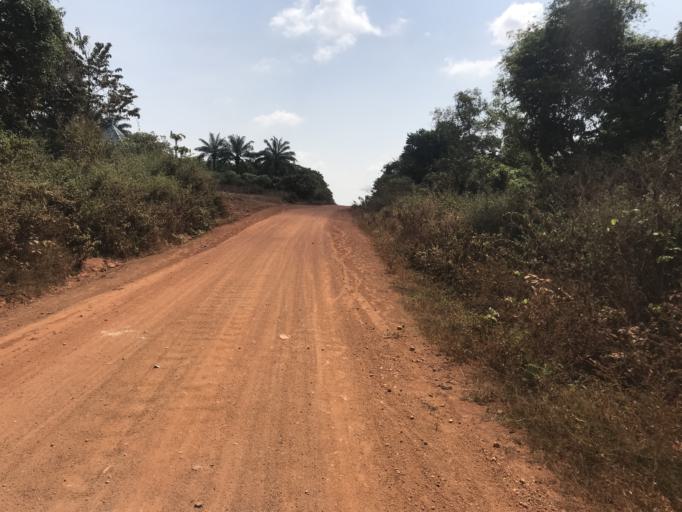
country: NG
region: Osun
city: Ifon
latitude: 7.8905
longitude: 4.4776
